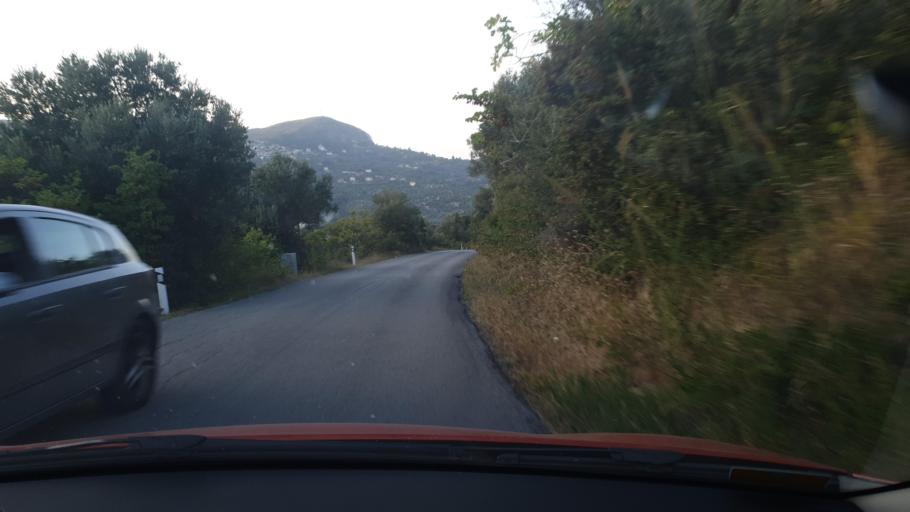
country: GR
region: Central Greece
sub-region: Nomos Evvoias
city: Oxilithos
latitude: 38.5982
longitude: 24.1164
